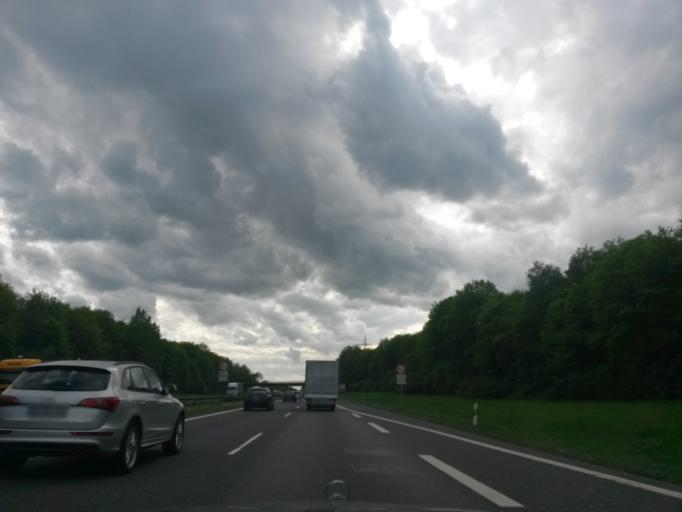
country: DE
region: Bavaria
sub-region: Regierungsbezirk Mittelfranken
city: Sachsen
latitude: 49.2568
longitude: 10.6593
